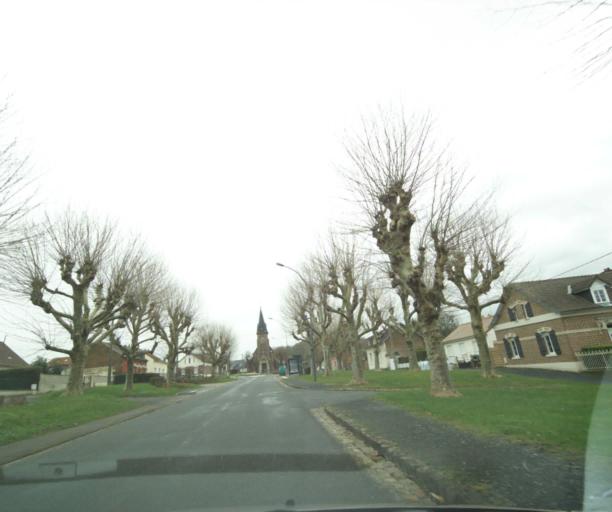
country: FR
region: Picardie
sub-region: Departement de l'Oise
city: Noyon
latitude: 49.5976
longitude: 3.0151
